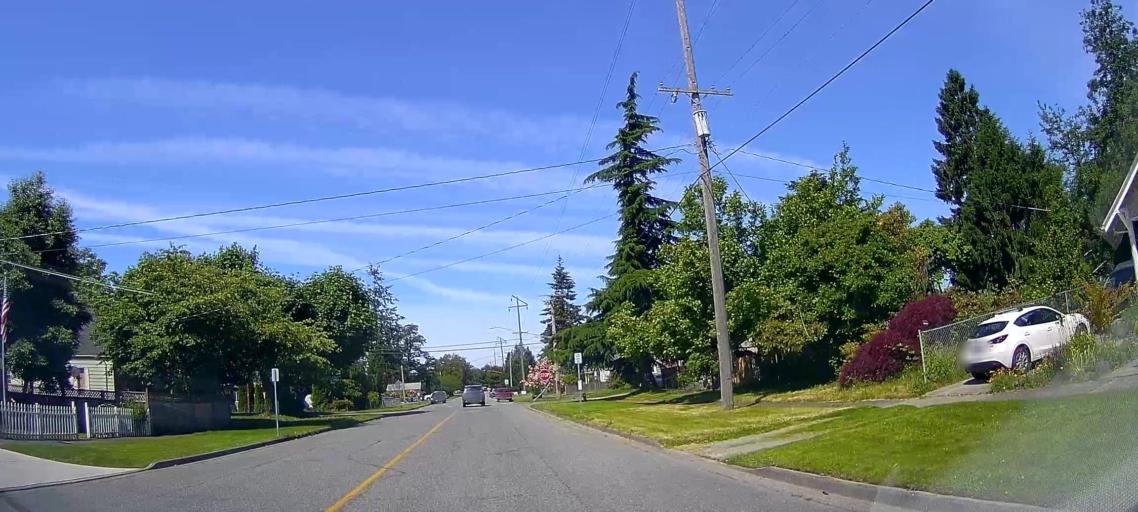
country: US
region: Washington
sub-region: Skagit County
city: Sedro-Woolley
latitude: 48.4989
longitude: -122.2290
